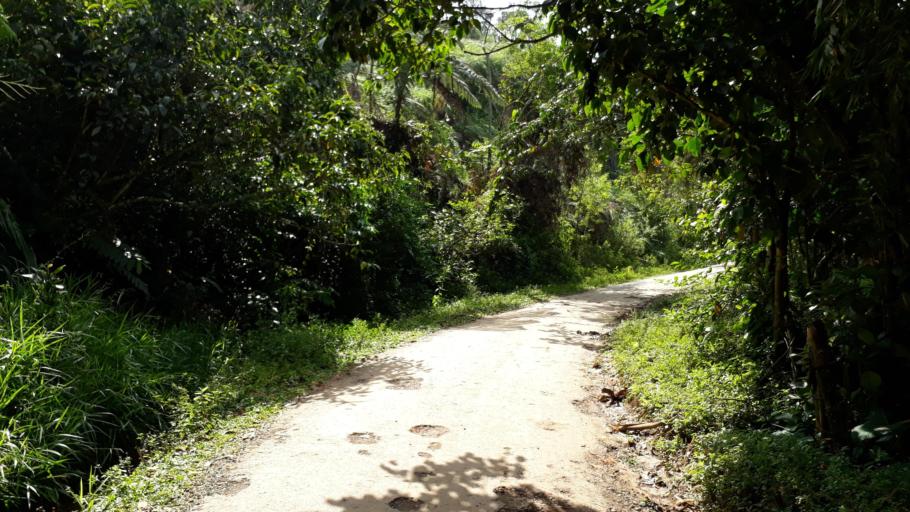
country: CO
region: Valle del Cauca
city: Jamundi
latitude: 3.2684
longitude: -76.6282
